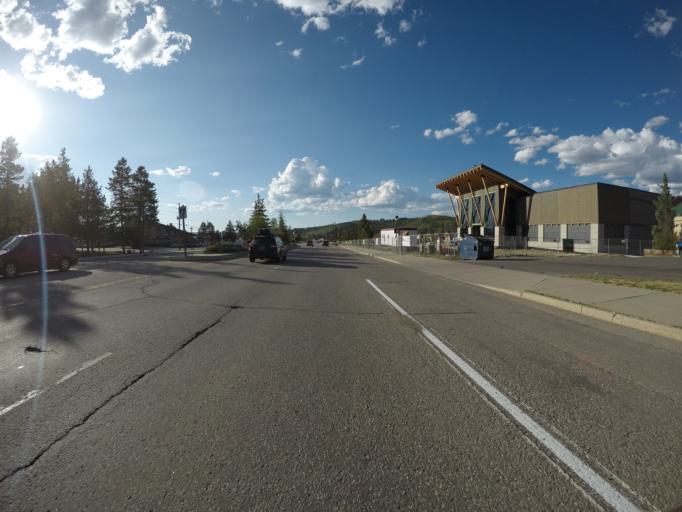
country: US
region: Colorado
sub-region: Grand County
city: Fraser
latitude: 39.9249
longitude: -105.7872
